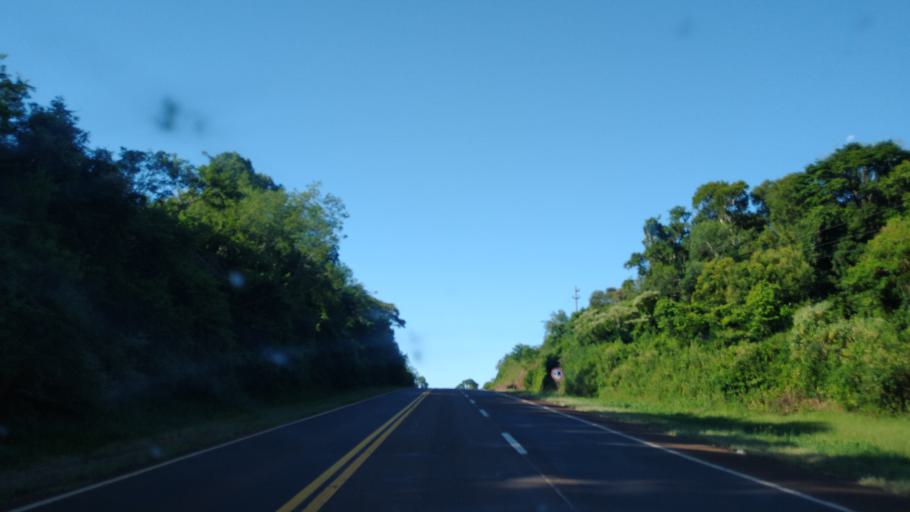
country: AR
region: Misiones
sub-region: Departamento de San Ignacio
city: San Ignacio
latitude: -27.2456
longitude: -55.5209
